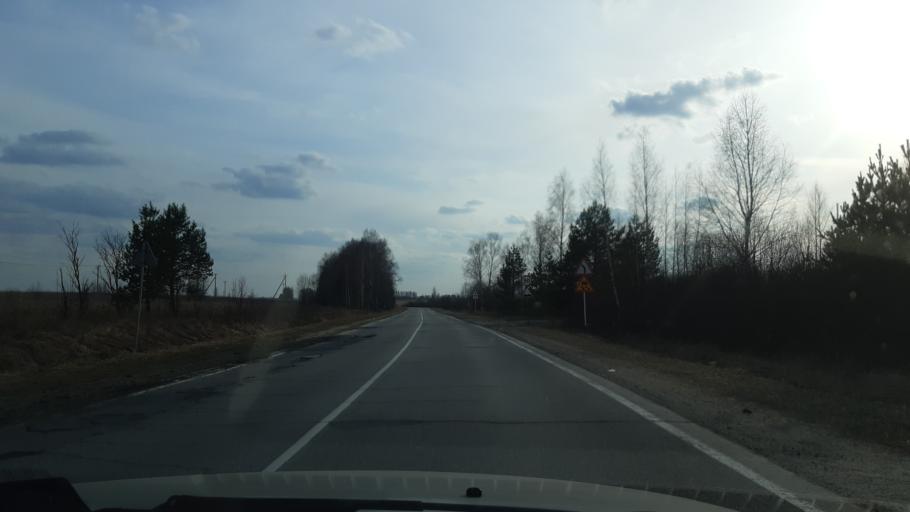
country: RU
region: Vladimir
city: Nikologory
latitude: 56.1751
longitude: 42.0040
